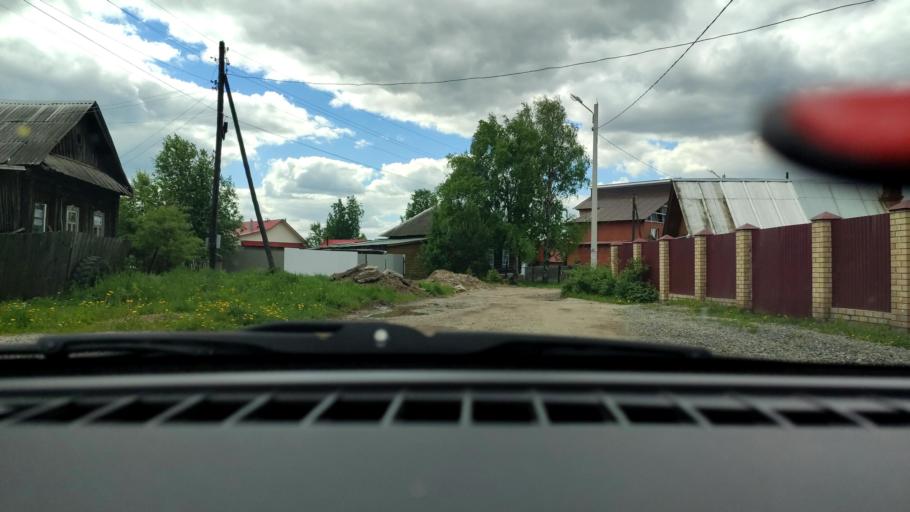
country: RU
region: Perm
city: Perm
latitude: 58.0464
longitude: 56.3614
